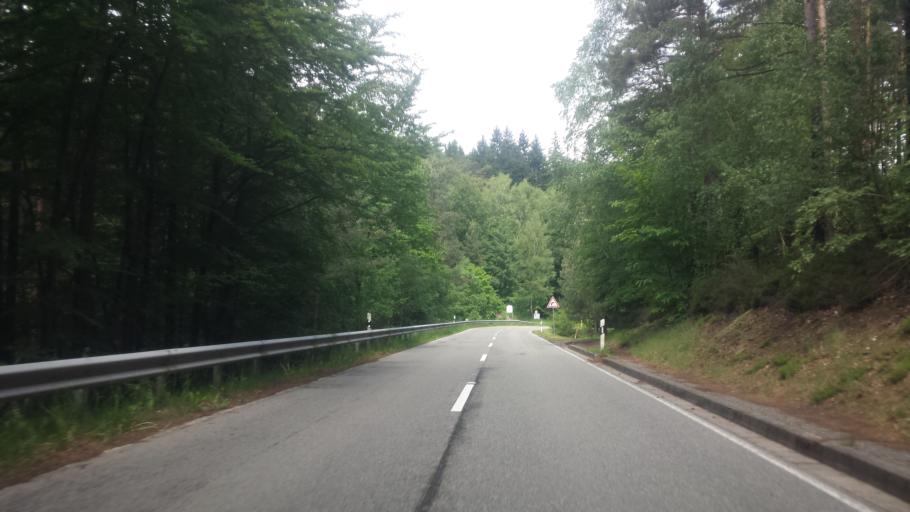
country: DE
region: Rheinland-Pfalz
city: Lindenberg
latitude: 49.3984
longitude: 8.1014
